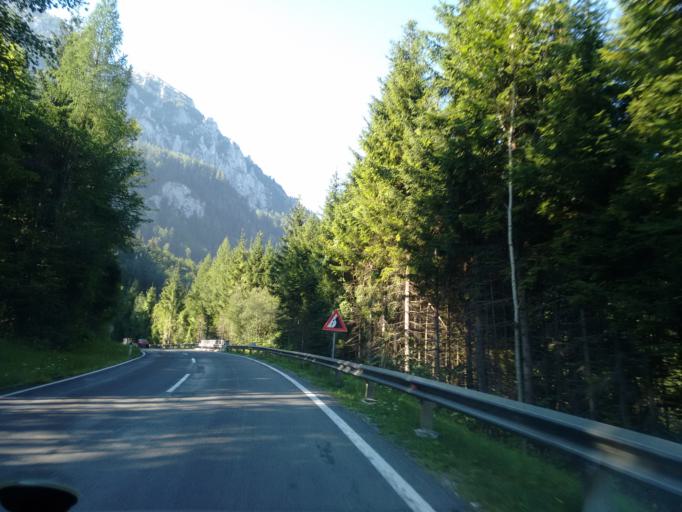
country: AT
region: Styria
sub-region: Politischer Bezirk Liezen
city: Ardning
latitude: 47.6342
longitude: 14.3267
